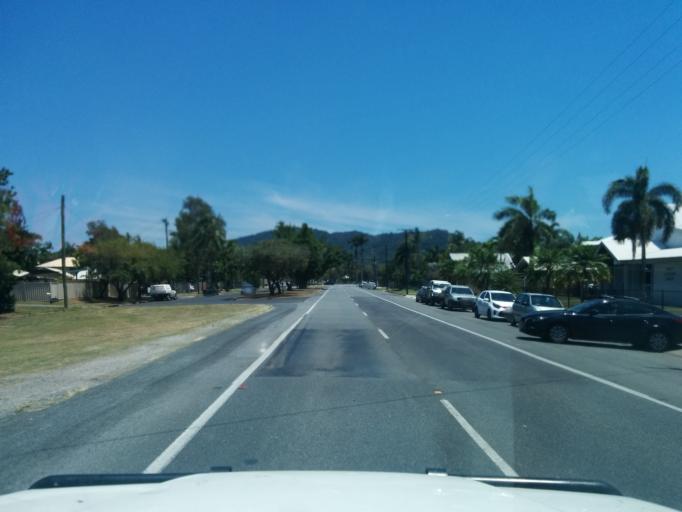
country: AU
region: Queensland
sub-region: Cairns
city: Cairns
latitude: -16.9148
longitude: 145.7562
